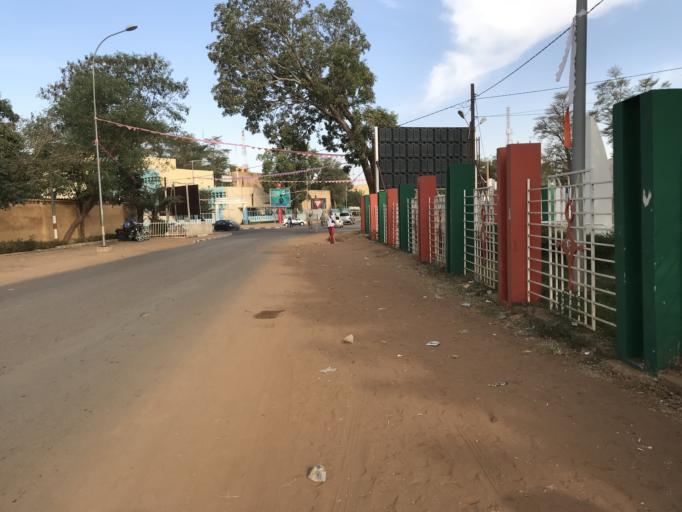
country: NE
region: Niamey
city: Niamey
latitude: 13.5078
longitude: 2.1152
